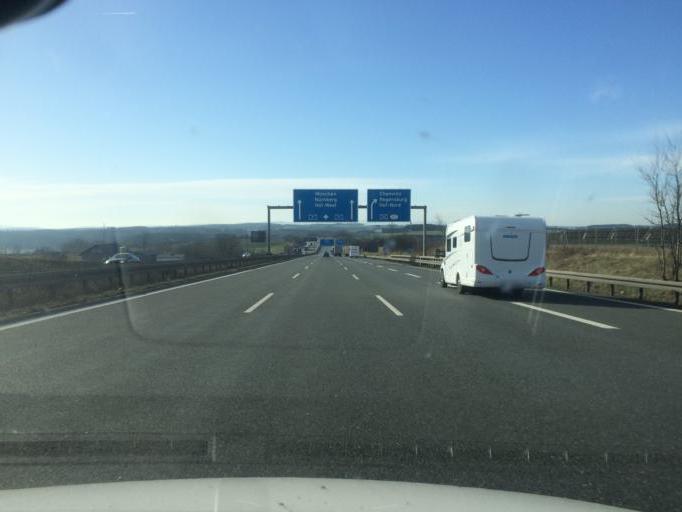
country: DE
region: Bavaria
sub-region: Upper Franconia
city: Leupoldsgrun
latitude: 50.3361
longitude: 11.7873
